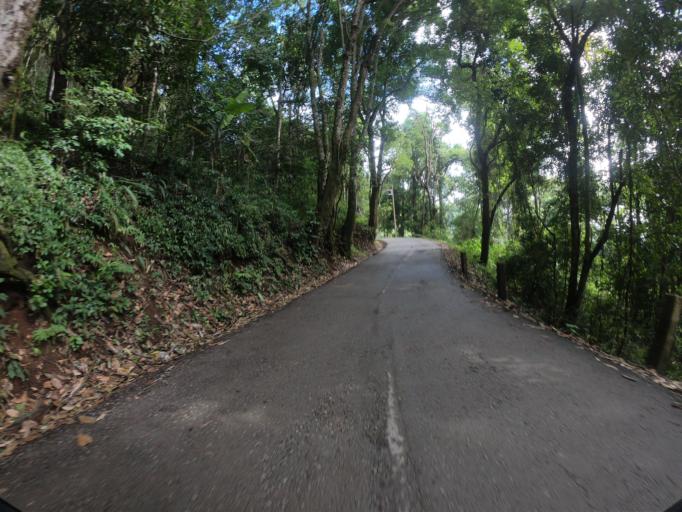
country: TH
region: Chiang Mai
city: Chiang Mai
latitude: 18.8139
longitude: 98.8828
